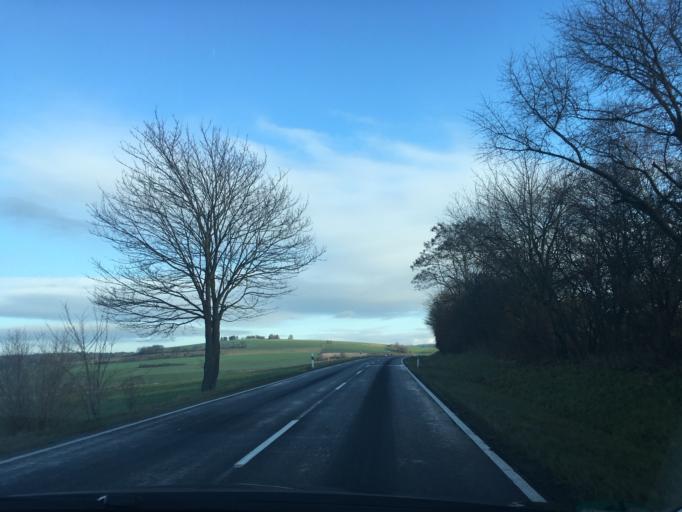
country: DE
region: Hesse
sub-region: Regierungsbezirk Kassel
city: Hofbieber
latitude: 50.5875
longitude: 9.8210
